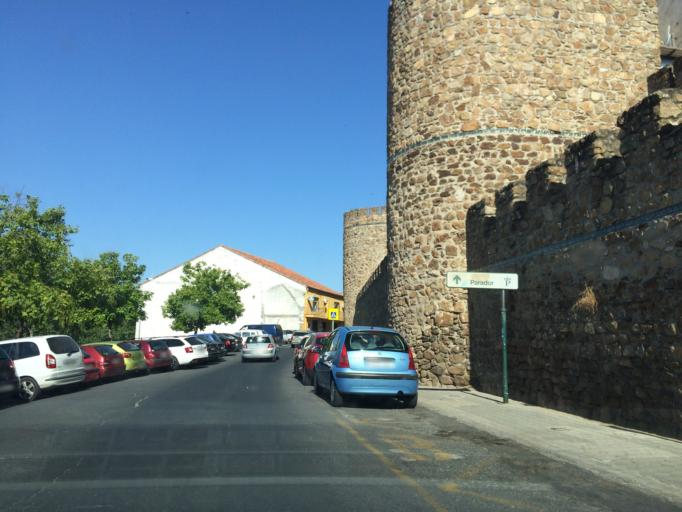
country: ES
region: Extremadura
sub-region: Provincia de Caceres
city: Plasencia
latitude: 40.0272
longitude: -6.0929
